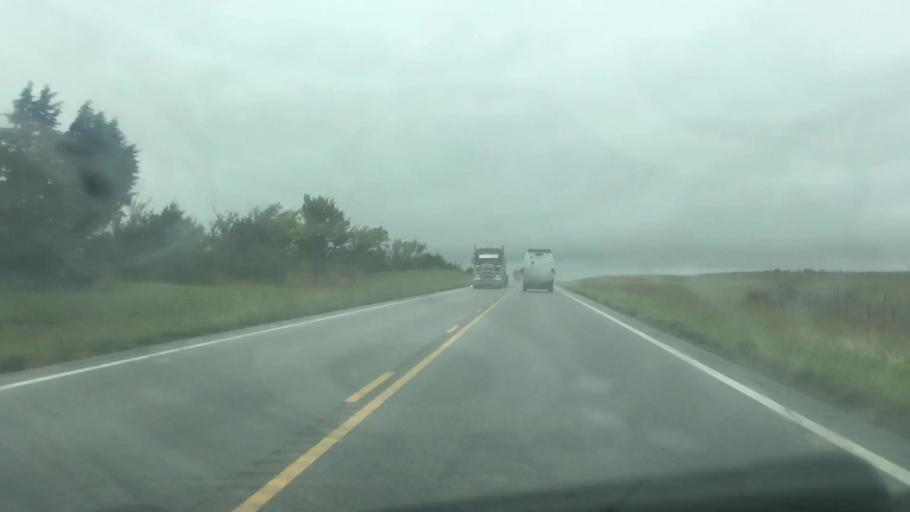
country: US
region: Kansas
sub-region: Anderson County
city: Garnett
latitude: 38.1490
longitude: -95.3207
